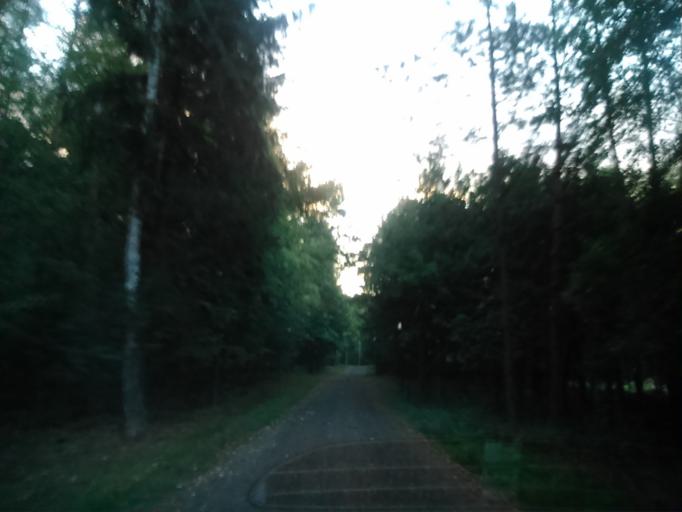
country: PL
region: Kujawsko-Pomorskie
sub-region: Powiat golubsko-dobrzynski
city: Radomin
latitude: 53.1629
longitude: 19.1417
